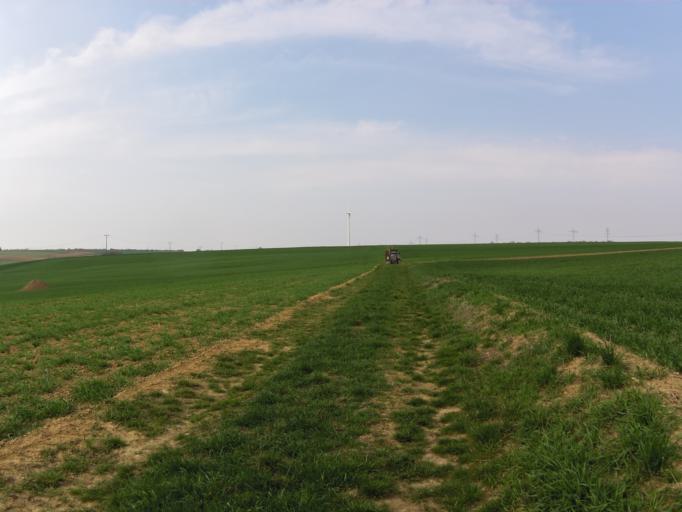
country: DE
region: Bavaria
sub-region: Regierungsbezirk Unterfranken
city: Theilheim
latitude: 49.7655
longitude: 10.0416
